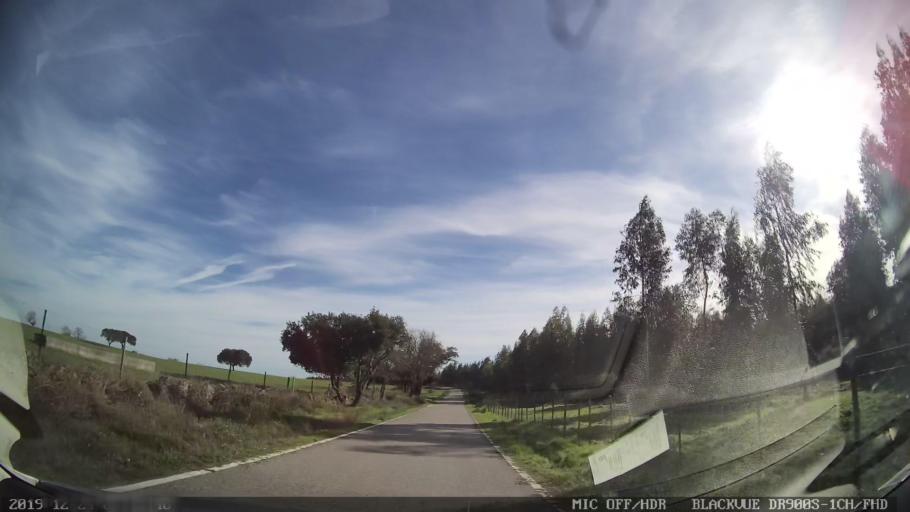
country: PT
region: Portalegre
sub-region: Nisa
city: Nisa
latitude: 39.4951
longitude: -7.7540
